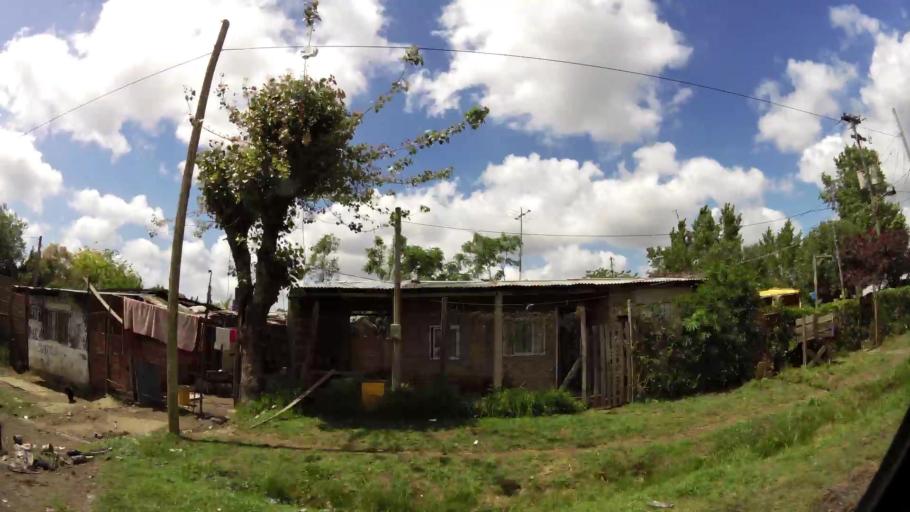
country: AR
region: Buenos Aires
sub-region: Partido de Quilmes
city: Quilmes
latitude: -34.8422
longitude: -58.2312
